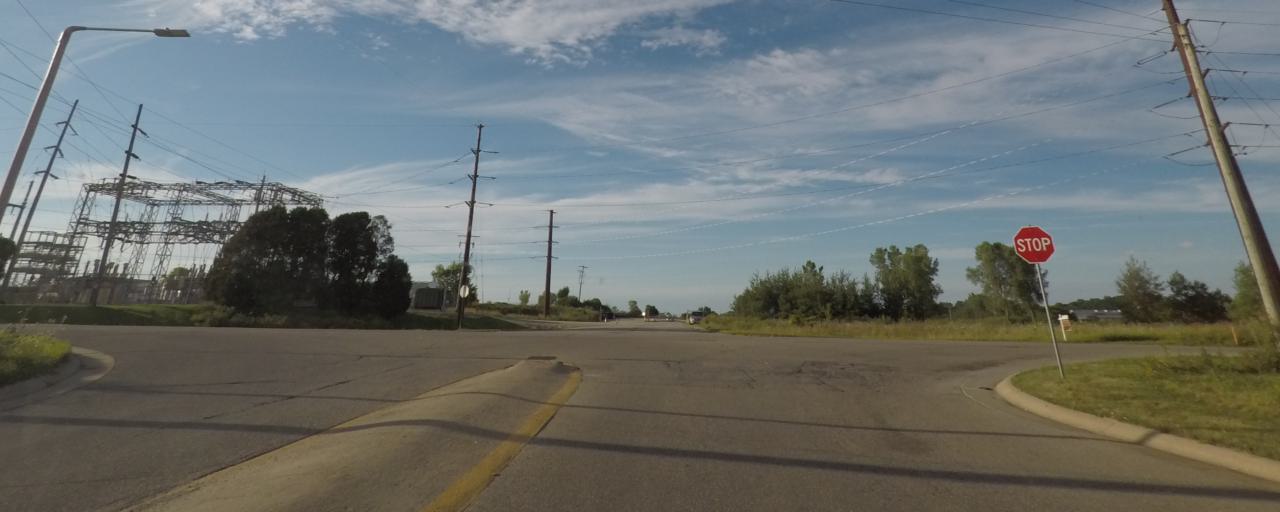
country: US
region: Wisconsin
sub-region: Dane County
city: Verona
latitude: 42.9721
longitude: -89.5139
